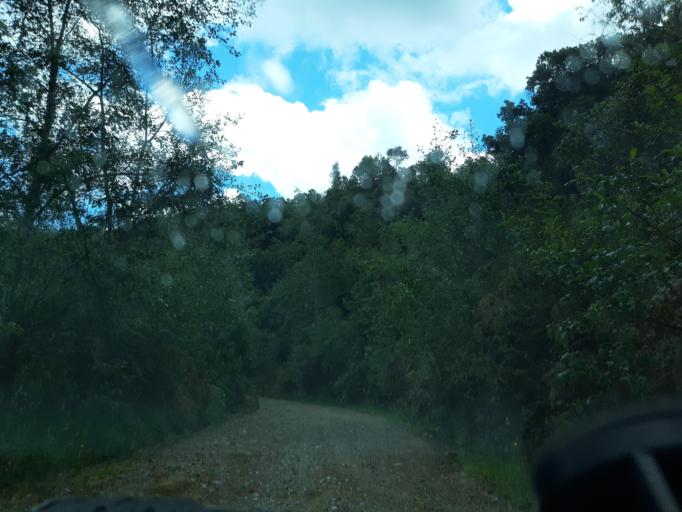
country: CO
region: Boyaca
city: Raquira
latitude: 5.5017
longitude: -73.6909
